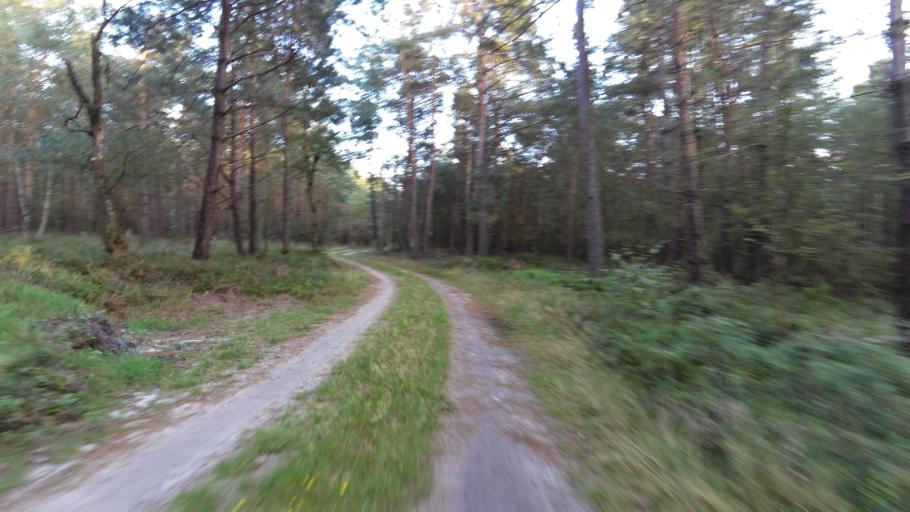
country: NL
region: Gelderland
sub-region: Gemeente Epe
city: Vaassen
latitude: 52.2765
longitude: 5.8902
